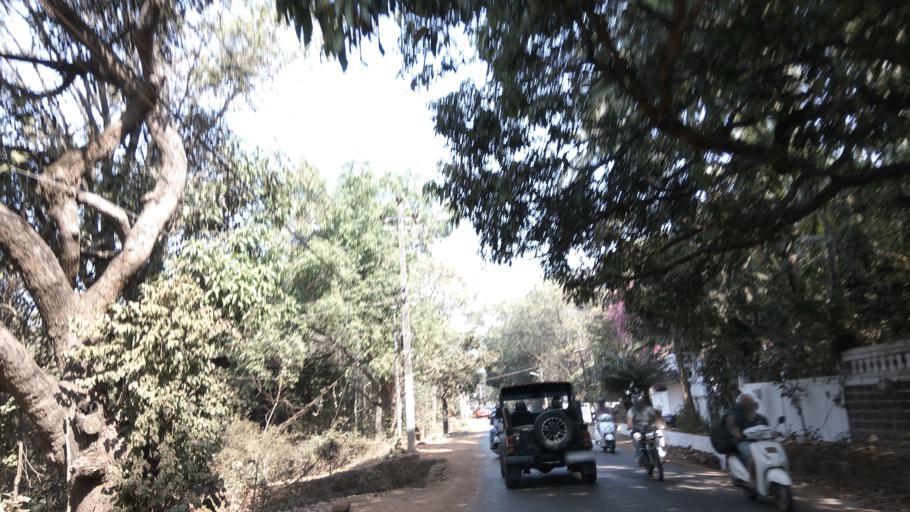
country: IN
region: Goa
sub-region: North Goa
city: Vagator
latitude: 15.5805
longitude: 73.7587
